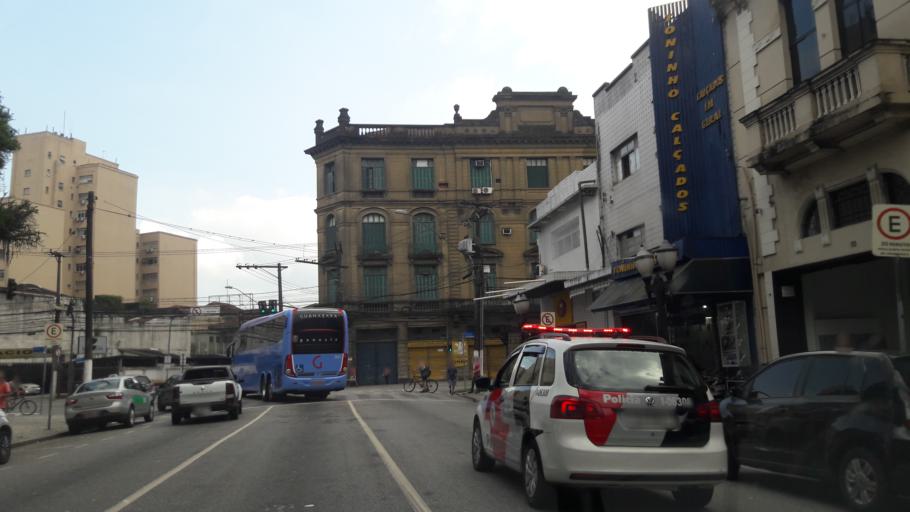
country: BR
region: Sao Paulo
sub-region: Santos
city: Santos
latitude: -23.9346
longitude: -46.3319
